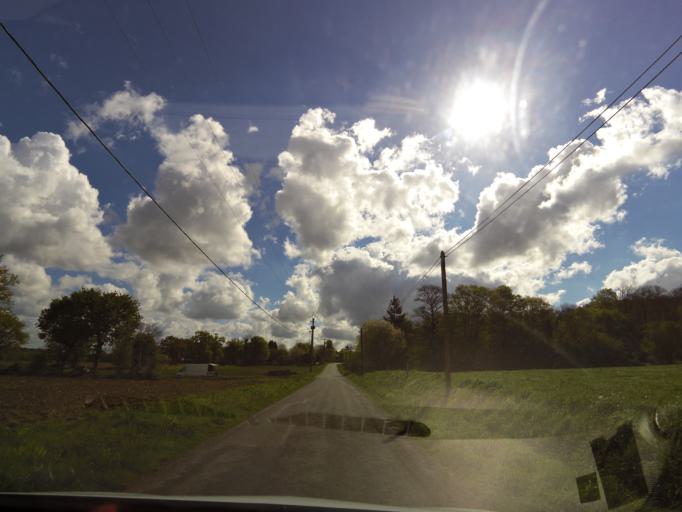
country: FR
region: Brittany
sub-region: Departement d'Ille-et-Vilaine
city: Orgeres
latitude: 47.9899
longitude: -1.6557
